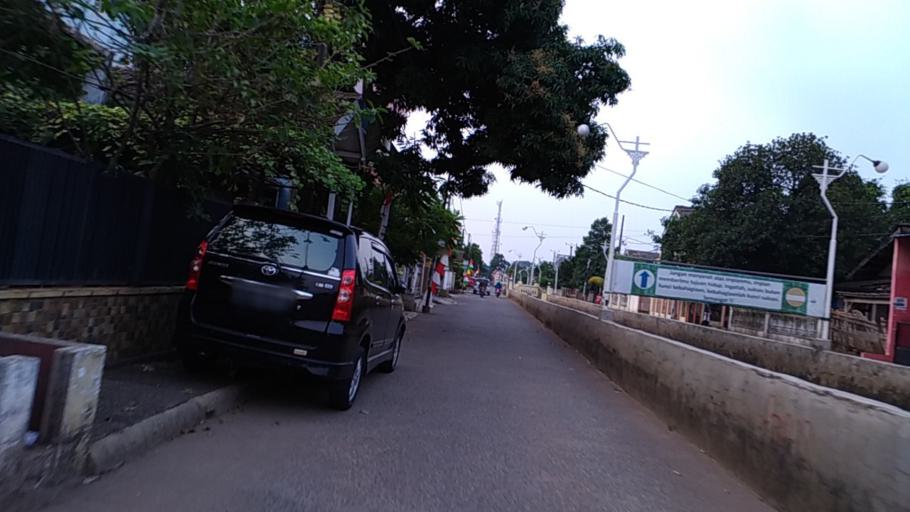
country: ID
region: West Java
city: Depok
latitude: -6.3754
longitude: 106.8584
